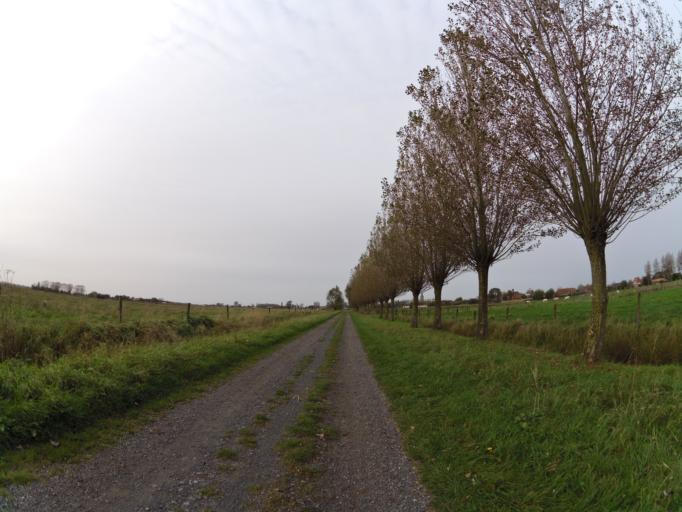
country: BE
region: Flanders
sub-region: Provincie West-Vlaanderen
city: Jabbeke
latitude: 51.2060
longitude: 3.0756
